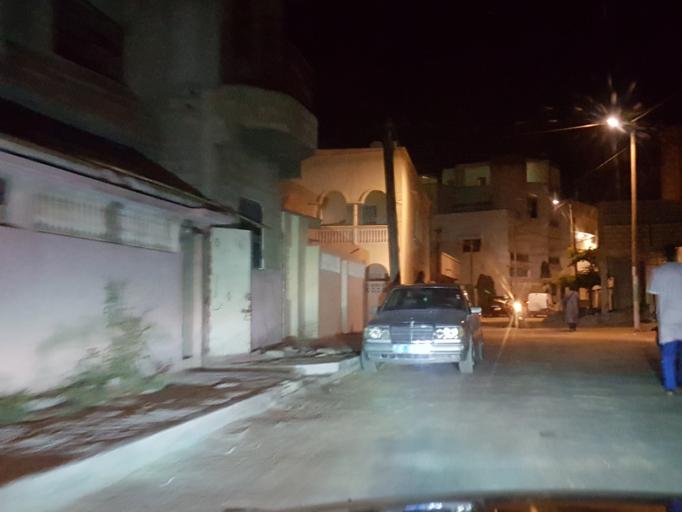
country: SN
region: Dakar
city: Grand Dakar
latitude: 14.7344
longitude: -17.4650
